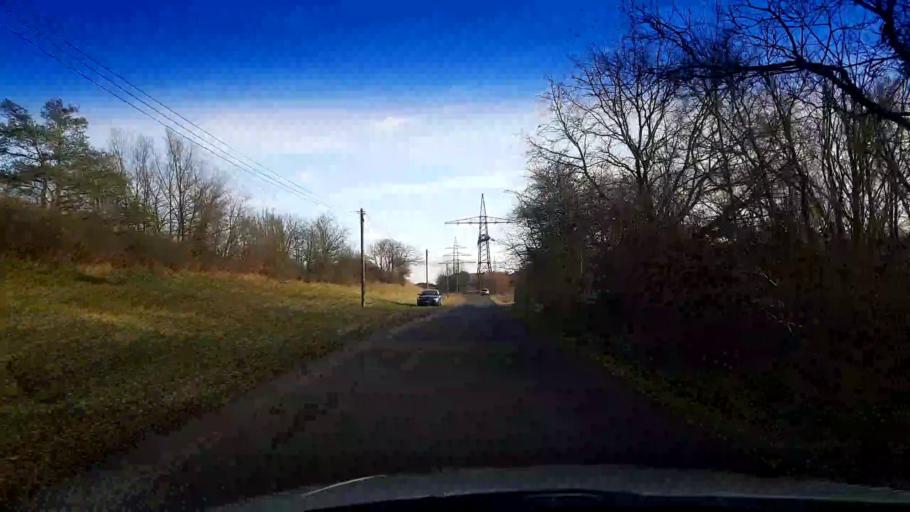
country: DE
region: Bavaria
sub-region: Upper Franconia
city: Strullendorf
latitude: 49.8348
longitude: 10.9599
